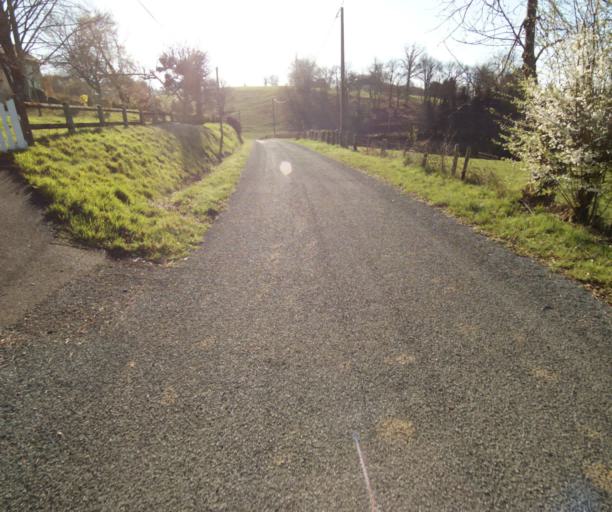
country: FR
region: Limousin
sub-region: Departement de la Correze
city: Seilhac
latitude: 45.3636
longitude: 1.7575
